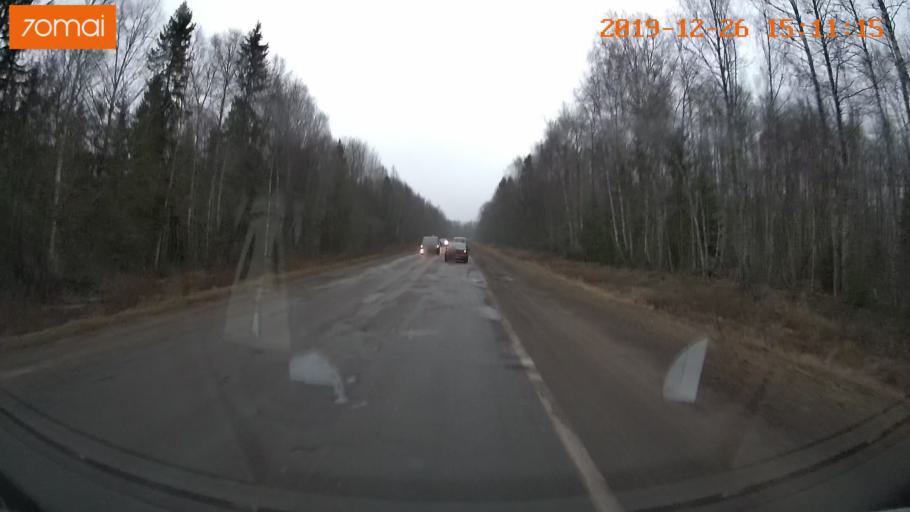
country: RU
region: Jaroslavl
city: Rybinsk
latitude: 58.1353
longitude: 38.8593
